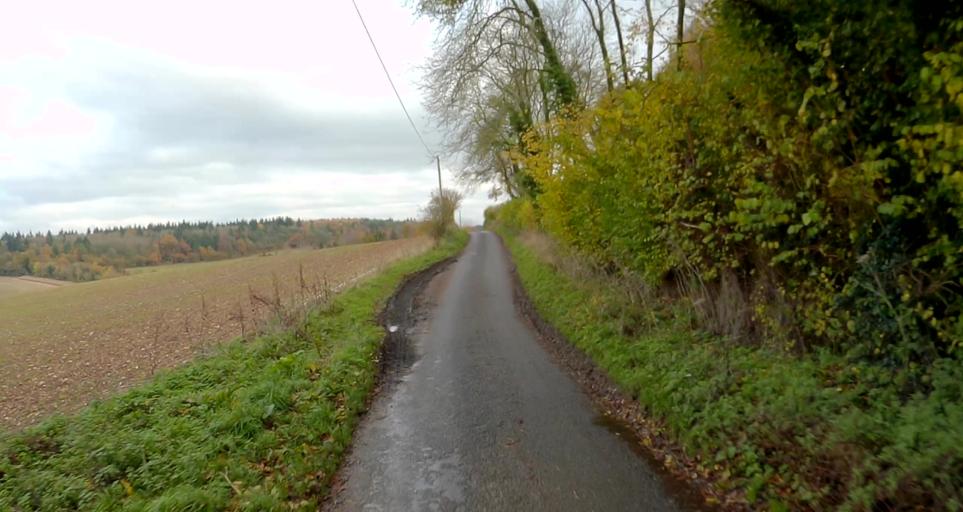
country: GB
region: England
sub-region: Hampshire
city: Long Sutton
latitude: 51.2135
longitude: -0.9604
